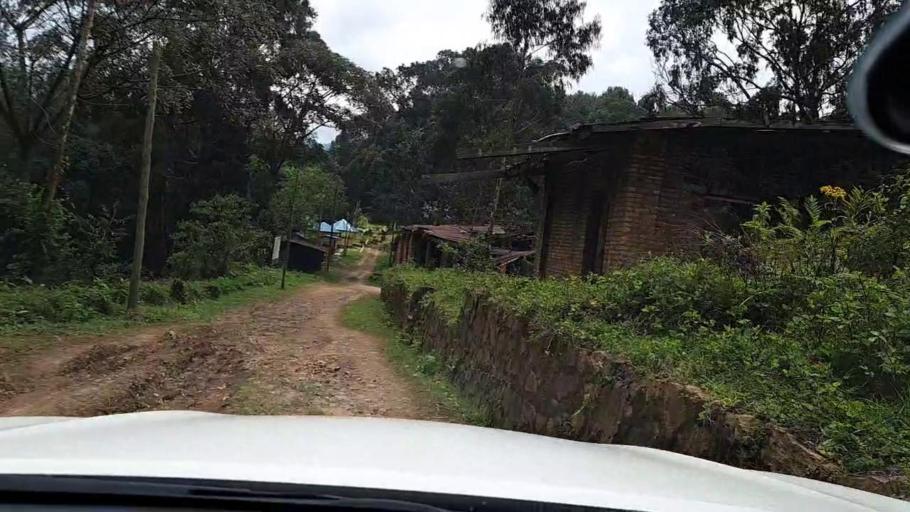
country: RW
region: Western Province
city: Kibuye
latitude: -2.2843
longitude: 29.3043
